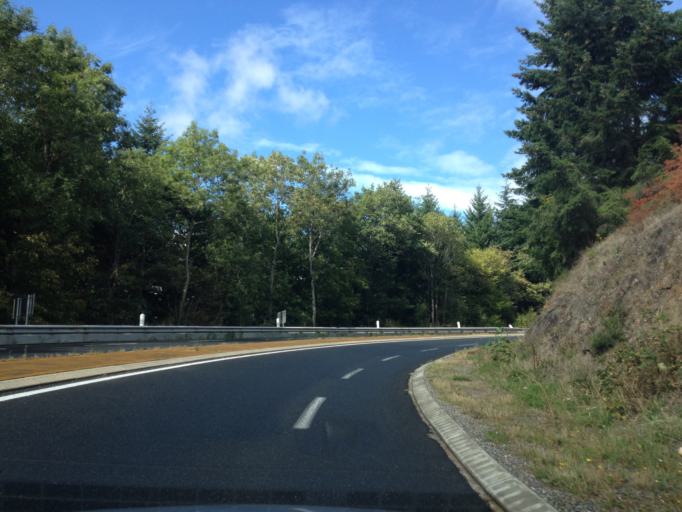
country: FR
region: Rhone-Alpes
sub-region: Departement de la Loire
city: Violay
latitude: 45.9041
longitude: 4.3601
